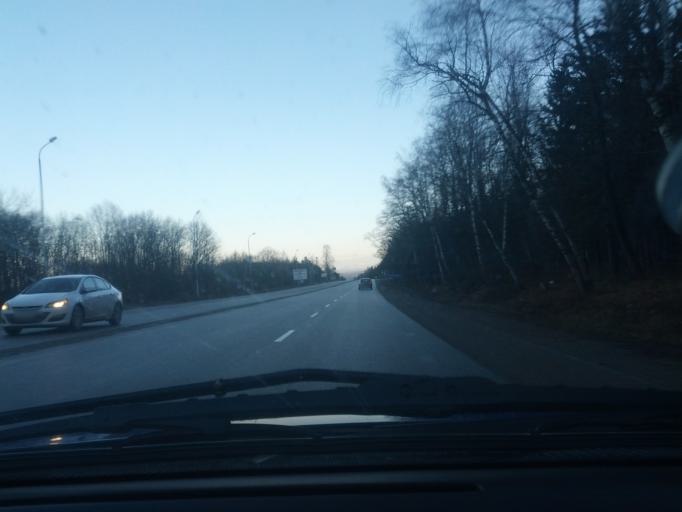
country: BG
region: Vratsa
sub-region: Obshtina Vratsa
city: Vratsa
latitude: 43.1834
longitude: 23.5897
